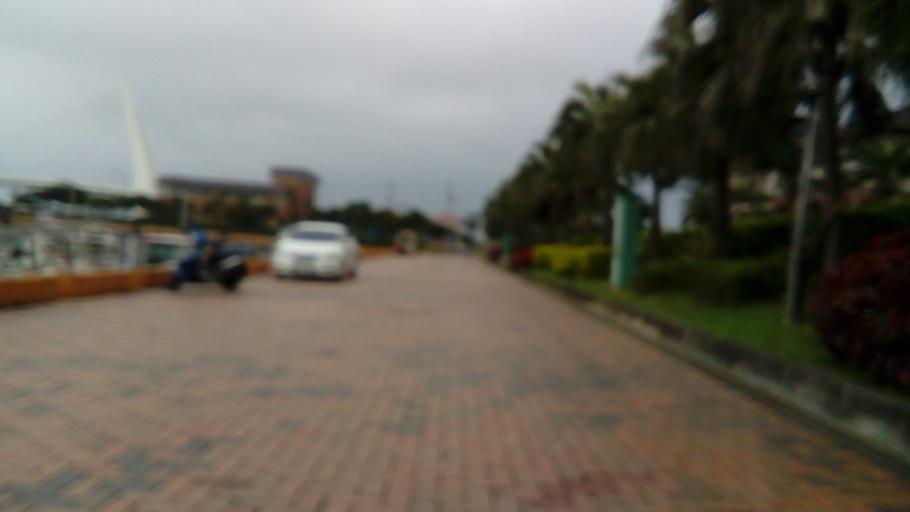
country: TW
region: Taipei
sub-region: Taipei
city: Banqiao
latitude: 25.1838
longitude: 121.4136
